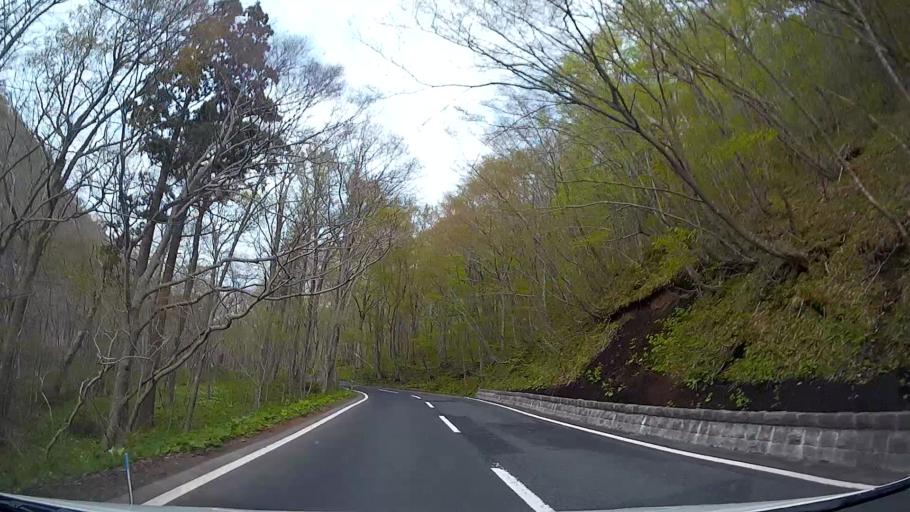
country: JP
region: Akita
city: Hanawa
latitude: 40.4791
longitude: 140.9433
